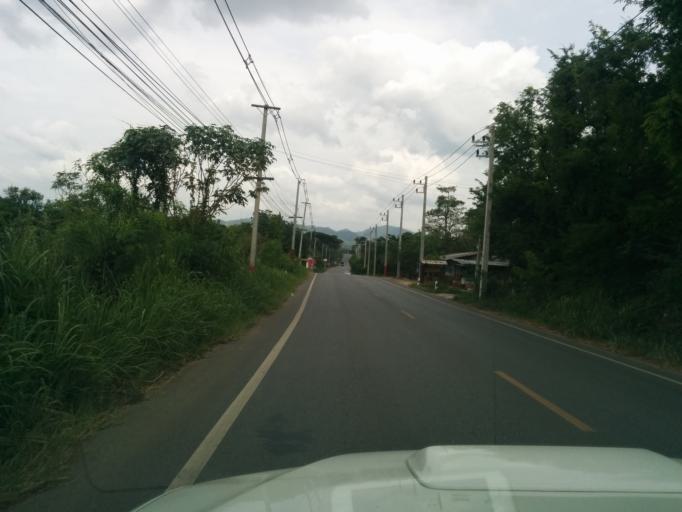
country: TH
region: Sara Buri
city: Muak Lek
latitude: 14.6164
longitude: 101.2123
